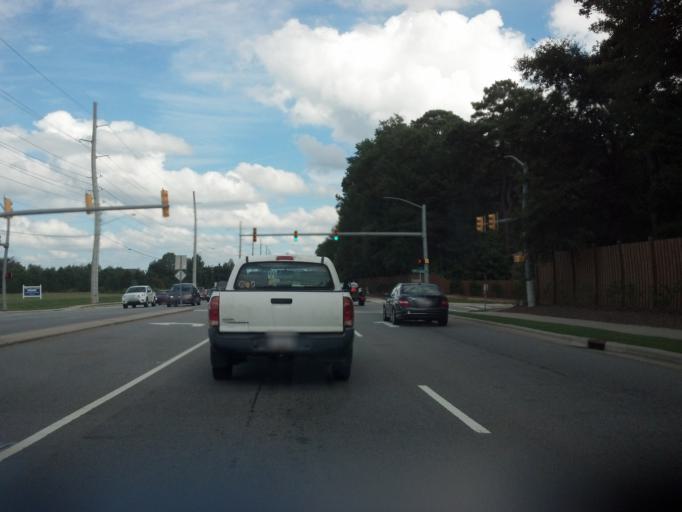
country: US
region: North Carolina
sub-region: Pitt County
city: Windsor
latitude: 35.5529
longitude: -77.3795
